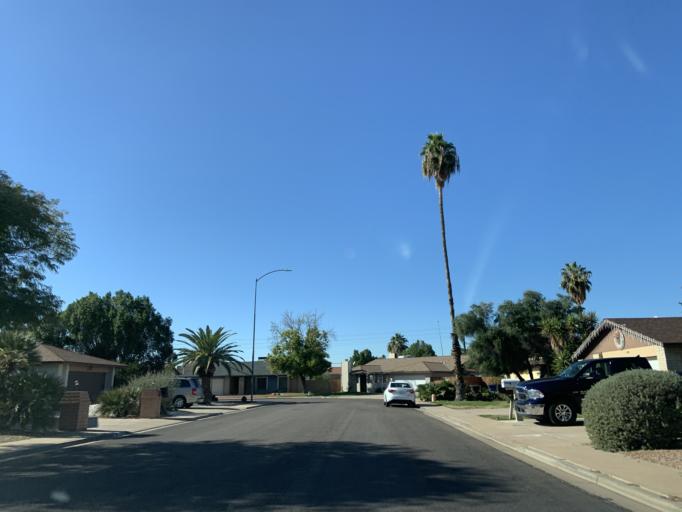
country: US
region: Arizona
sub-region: Maricopa County
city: San Carlos
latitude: 33.3623
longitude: -111.8579
